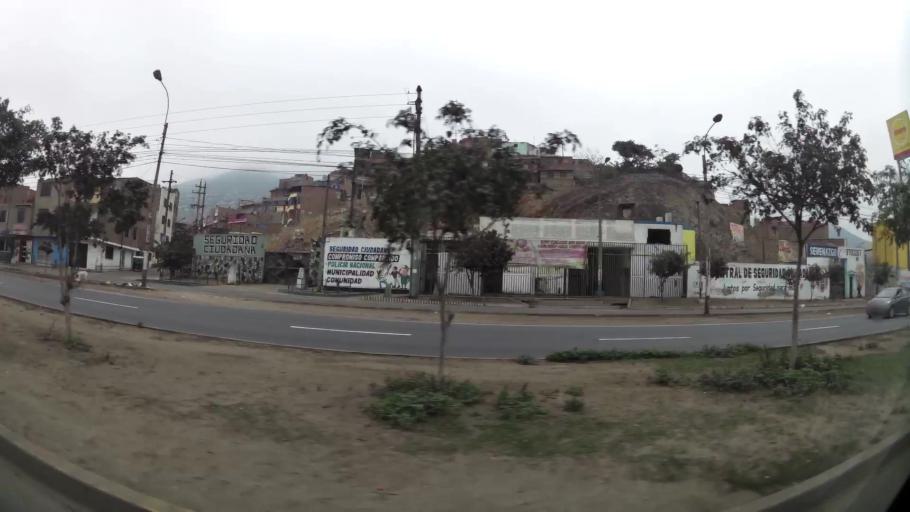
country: PE
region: Lima
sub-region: Lima
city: Urb. Santo Domingo
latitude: -11.9307
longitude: -77.0443
